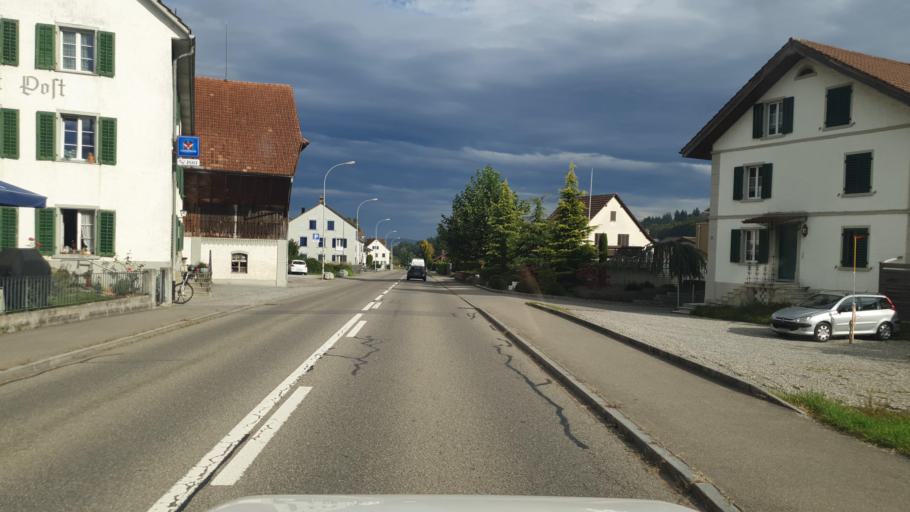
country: CH
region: Aargau
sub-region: Bezirk Bremgarten
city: Sarmenstorf
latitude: 47.3124
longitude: 8.2466
